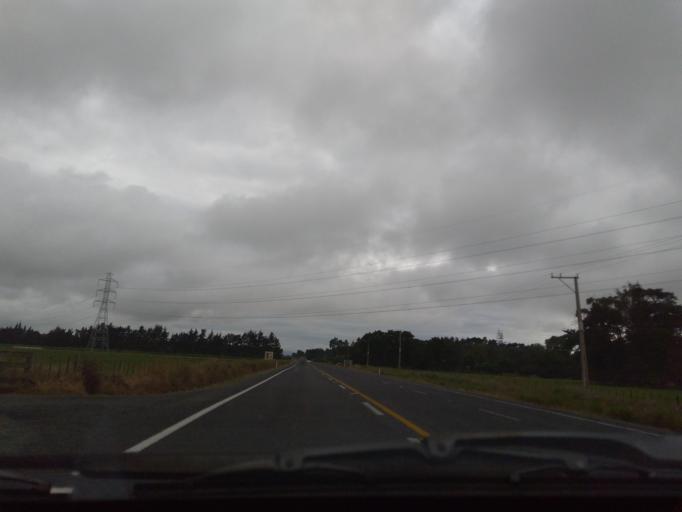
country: NZ
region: Northland
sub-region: Whangarei
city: Ruakaka
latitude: -35.9907
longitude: 174.4238
